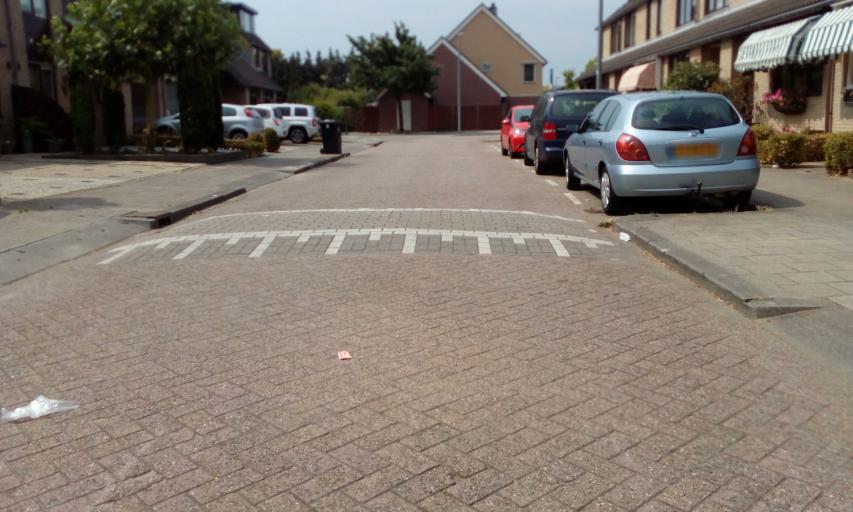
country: NL
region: South Holland
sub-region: Gemeente Capelle aan den IJssel
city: Capelle aan den IJssel
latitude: 51.9707
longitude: 4.5814
